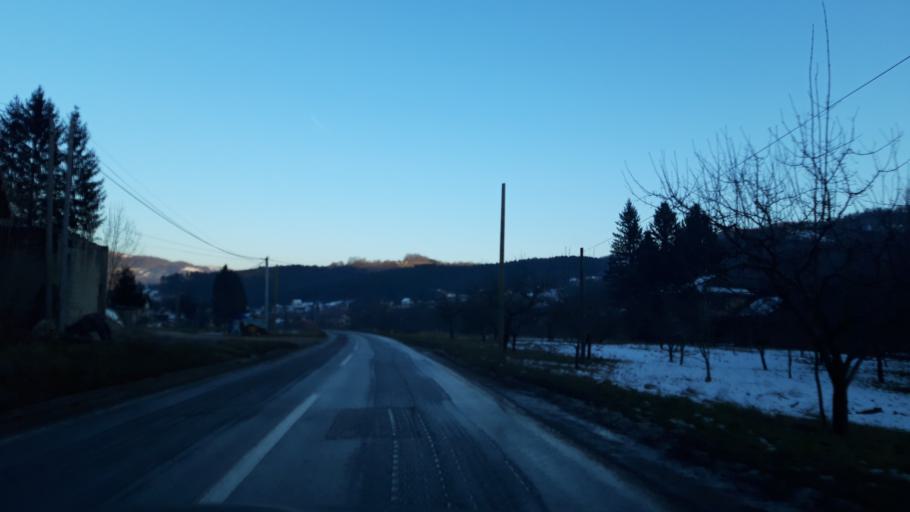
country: BA
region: Republika Srpska
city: Milici
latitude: 44.1636
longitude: 19.0622
